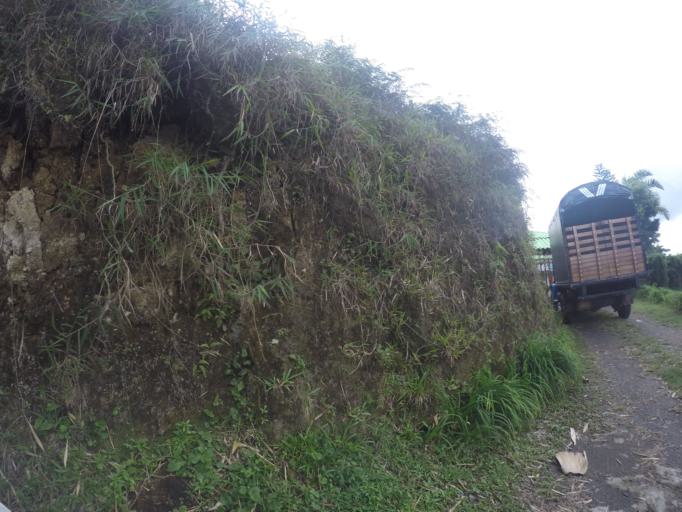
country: CO
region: Quindio
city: Filandia
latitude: 4.6797
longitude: -75.6571
